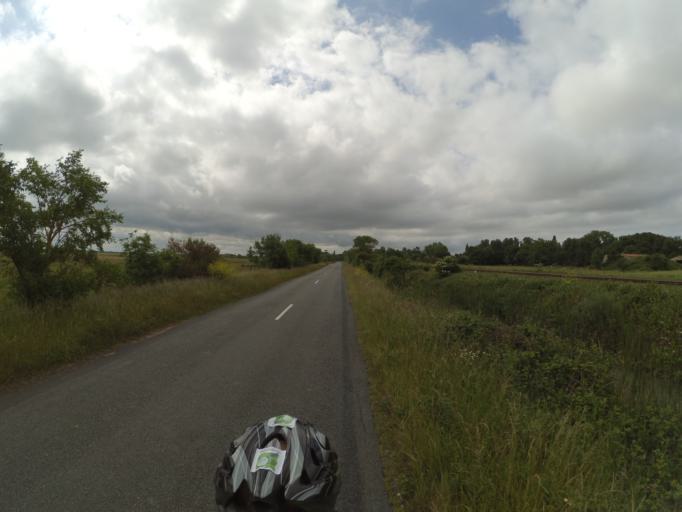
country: FR
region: Poitou-Charentes
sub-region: Departement de la Charente-Maritime
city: Yves
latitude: 46.0249
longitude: -1.0473
